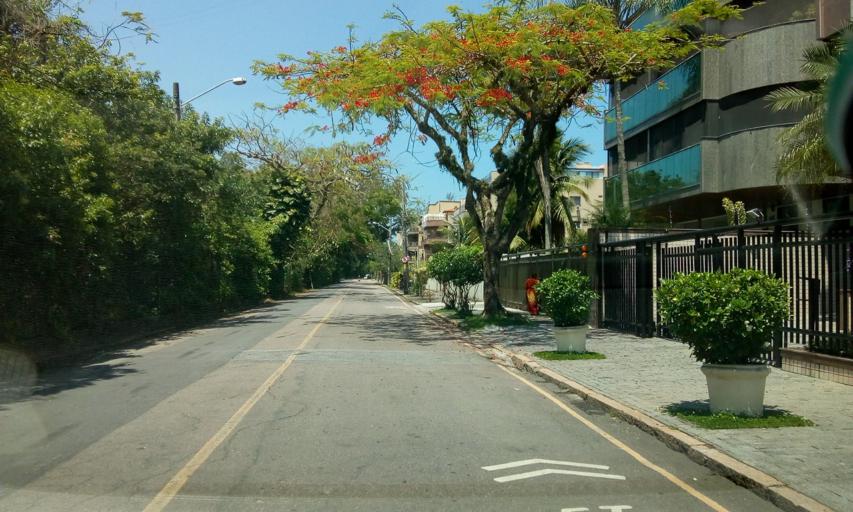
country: BR
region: Rio de Janeiro
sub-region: Nilopolis
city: Nilopolis
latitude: -23.0241
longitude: -43.4620
